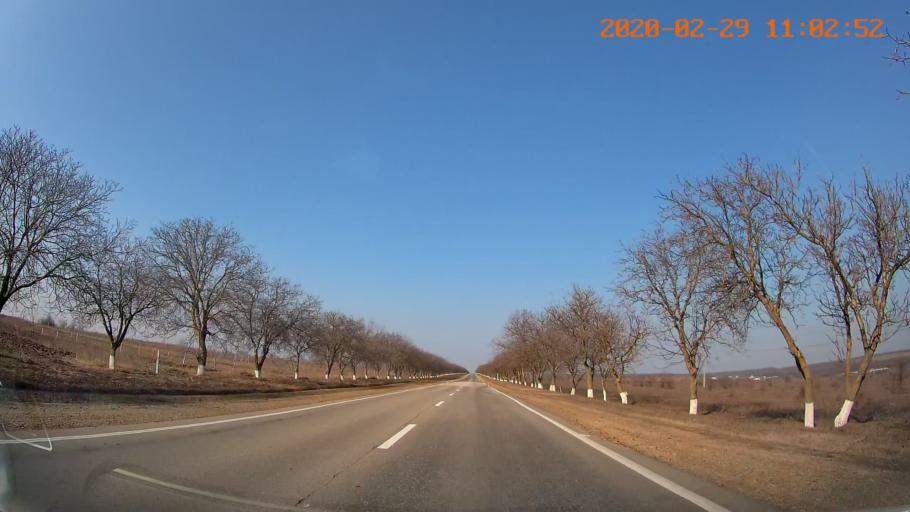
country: MD
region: Telenesti
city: Grigoriopol
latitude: 47.1755
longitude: 29.2294
